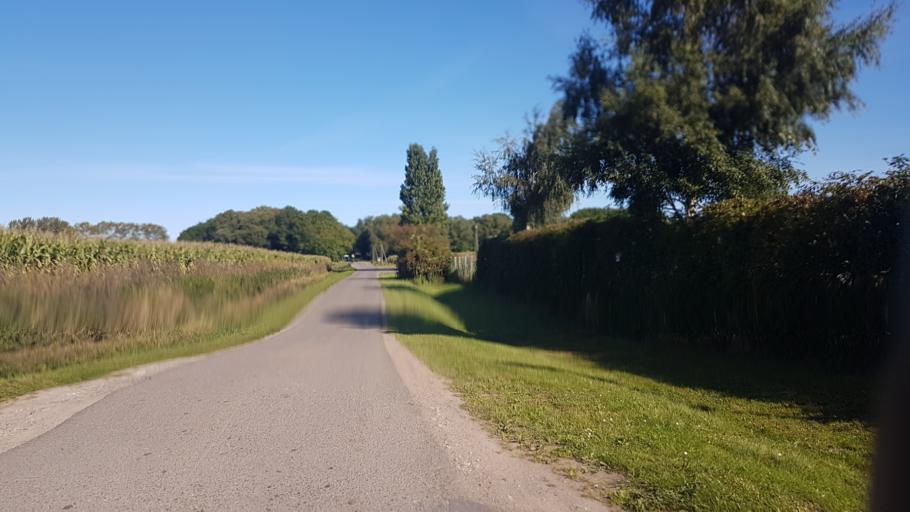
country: DE
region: Mecklenburg-Vorpommern
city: Sagard
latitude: 54.5163
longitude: 13.5304
